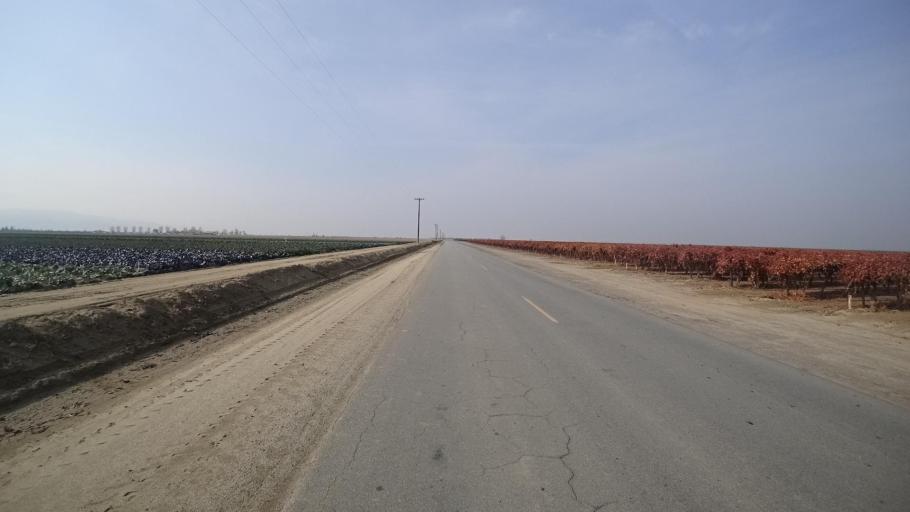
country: US
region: California
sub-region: Kern County
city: Weedpatch
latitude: 35.0753
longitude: -118.9466
